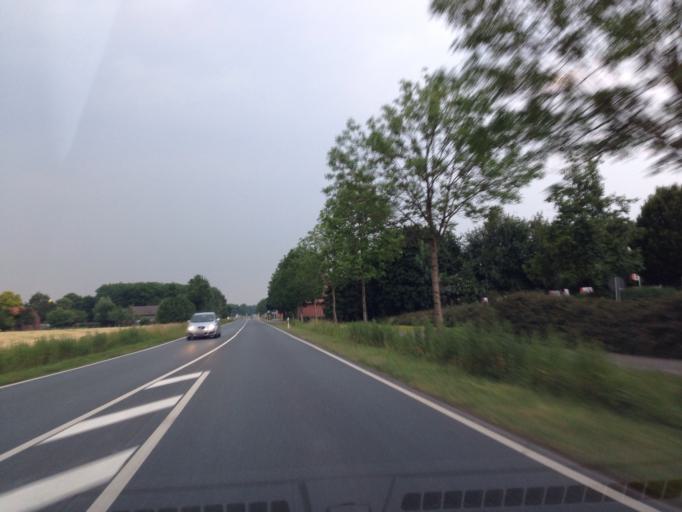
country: DE
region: North Rhine-Westphalia
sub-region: Regierungsbezirk Munster
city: Nottuln
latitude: 51.9145
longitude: 7.3887
